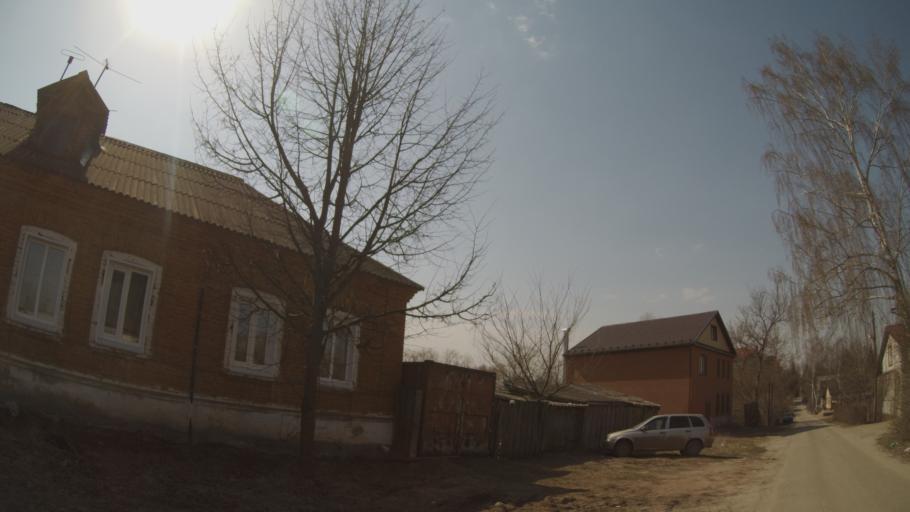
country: RU
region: Nizjnij Novgorod
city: Arzamas
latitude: 55.3909
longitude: 43.8226
